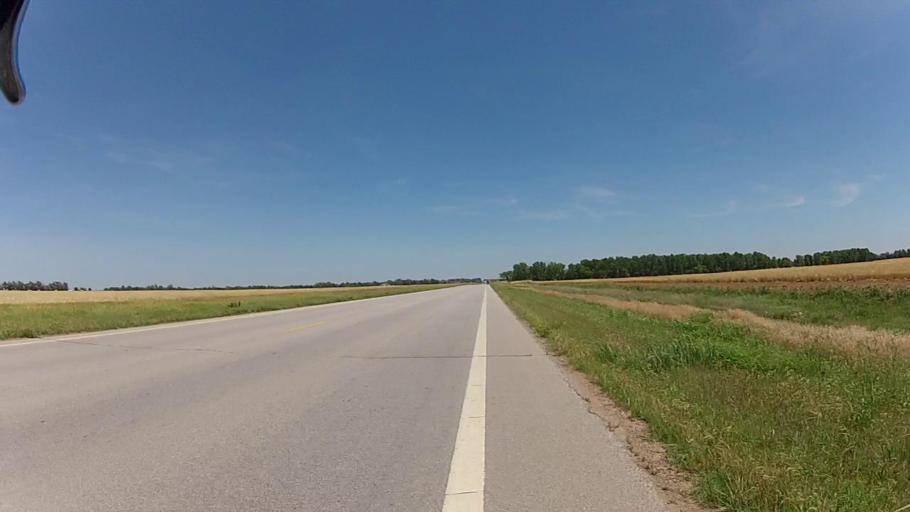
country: US
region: Kansas
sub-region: Harper County
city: Harper
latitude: 37.2386
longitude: -98.1367
